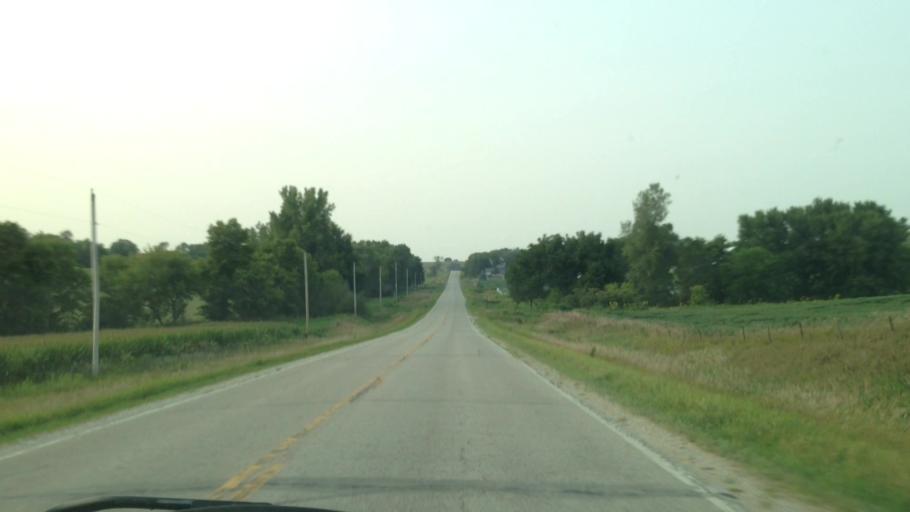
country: US
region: Iowa
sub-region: Iowa County
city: Marengo
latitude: 41.8711
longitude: -92.0889
